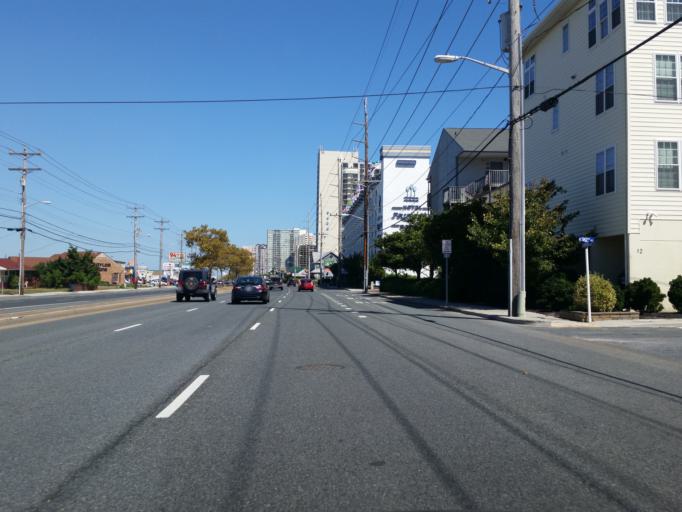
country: US
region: Maryland
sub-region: Worcester County
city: Ocean City
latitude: 38.4064
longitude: -75.0593
